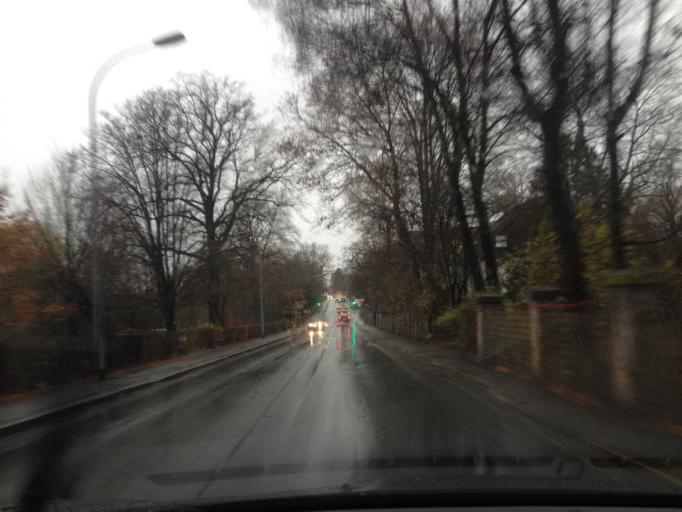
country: DE
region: Bavaria
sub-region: Regierungsbezirk Mittelfranken
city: Lauf an der Pegnitz
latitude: 49.5130
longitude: 11.2778
